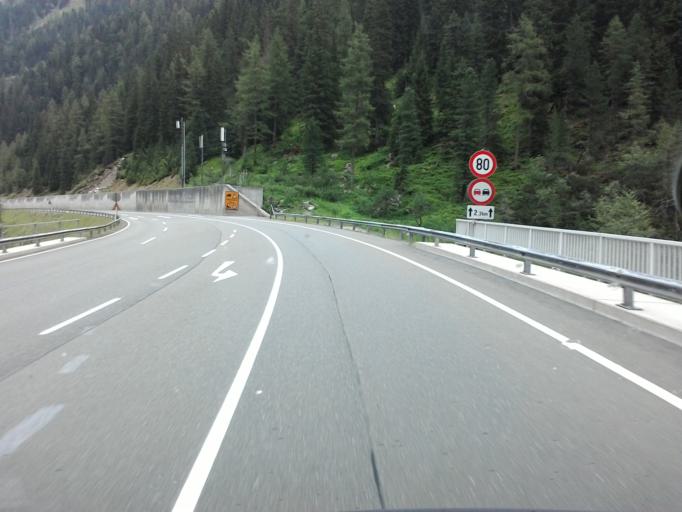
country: AT
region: Salzburg
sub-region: Politischer Bezirk Zell am See
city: Stuhlfelden
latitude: 47.1605
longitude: 12.5361
